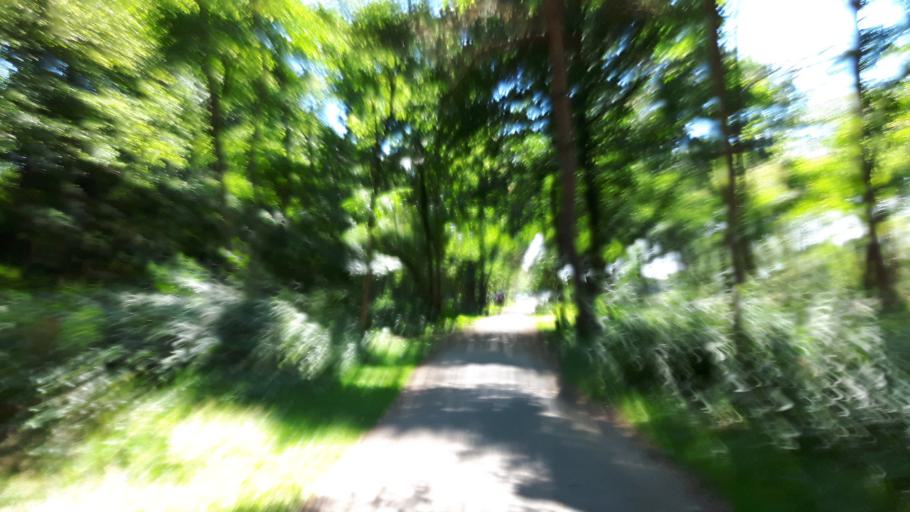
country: NL
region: North Holland
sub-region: Gemeente Wijdemeren
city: Nieuw-Loosdrecht
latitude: 52.1961
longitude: 5.1559
